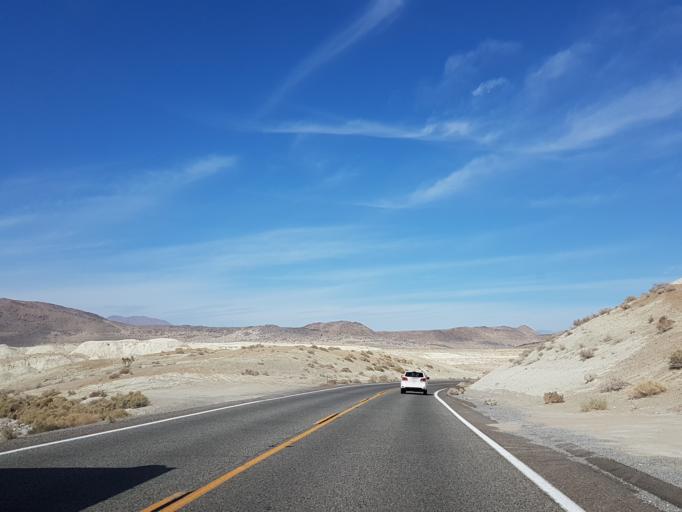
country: US
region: California
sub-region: San Bernardino County
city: Searles Valley
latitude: 35.6660
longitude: -117.4271
